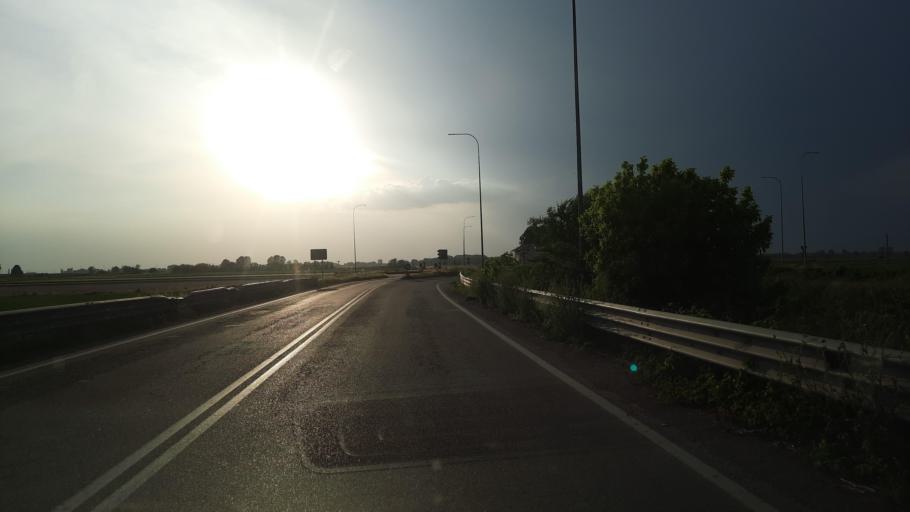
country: IT
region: Lombardy
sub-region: Provincia di Pavia
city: Cergnago
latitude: 45.2393
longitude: 8.7856
